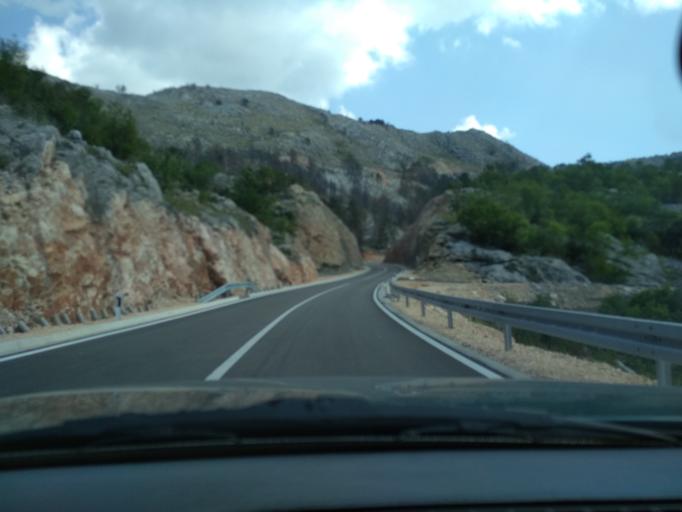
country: ME
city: Dobrota
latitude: 42.4376
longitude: 18.8366
